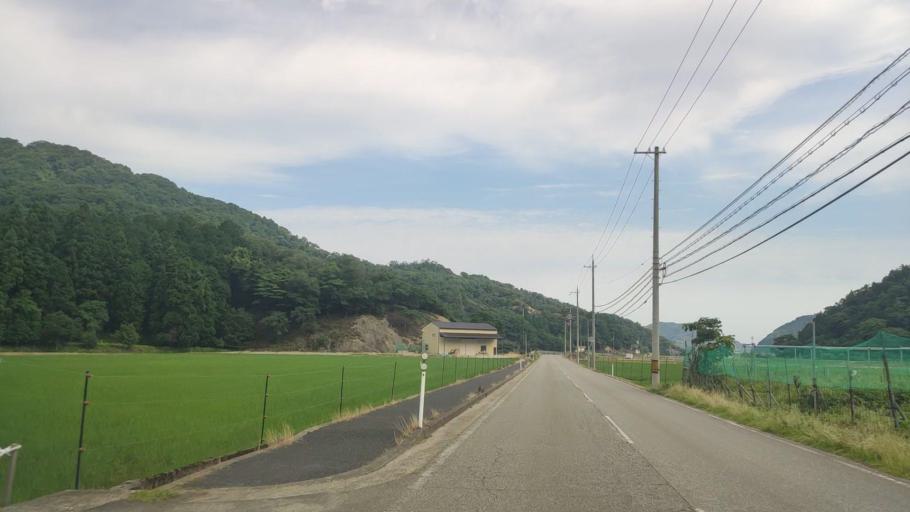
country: JP
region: Hyogo
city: Toyooka
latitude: 35.6191
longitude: 134.8423
